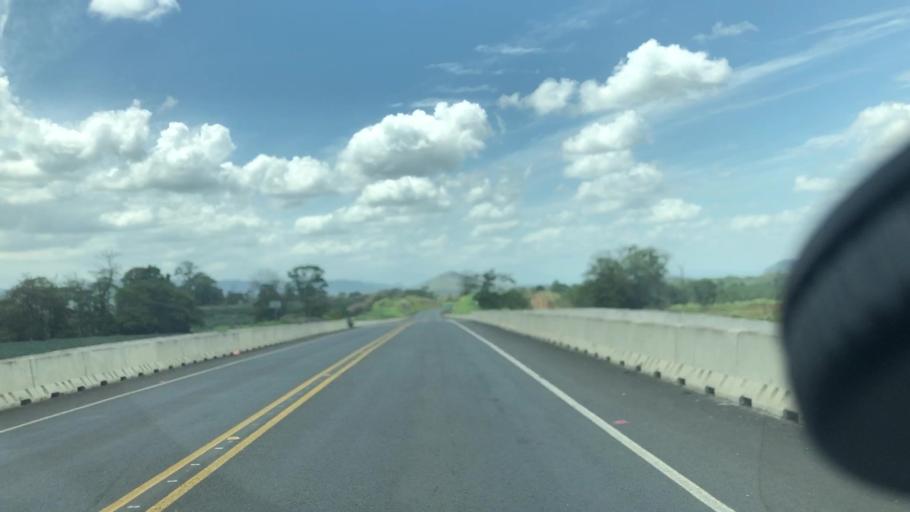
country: CR
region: Alajuela
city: Pital
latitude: 10.4345
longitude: -84.2780
